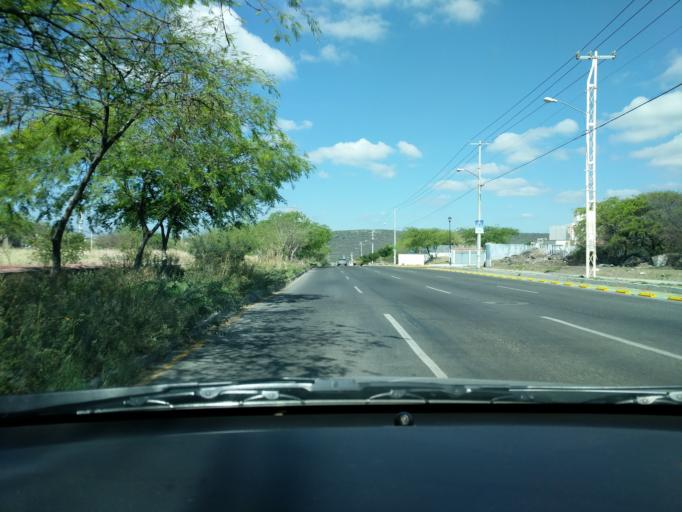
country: MX
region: Queretaro
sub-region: Queretaro
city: Patria Nueva
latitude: 20.6440
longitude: -100.4875
